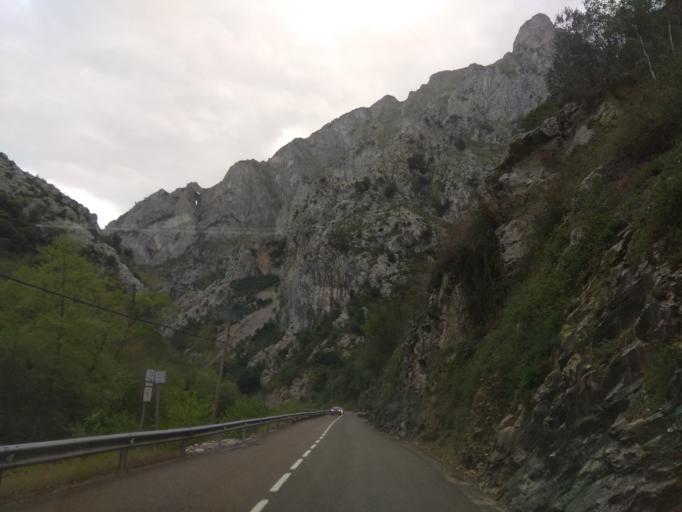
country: ES
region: Cantabria
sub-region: Provincia de Cantabria
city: Tresviso
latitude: 43.2766
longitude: -4.6358
